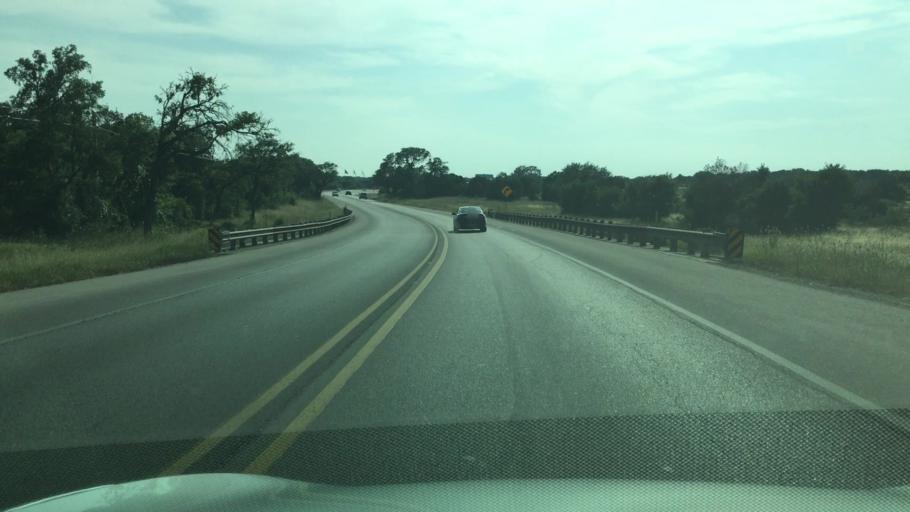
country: US
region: Texas
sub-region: Hays County
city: Wimberley
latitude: 29.9176
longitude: -98.0432
